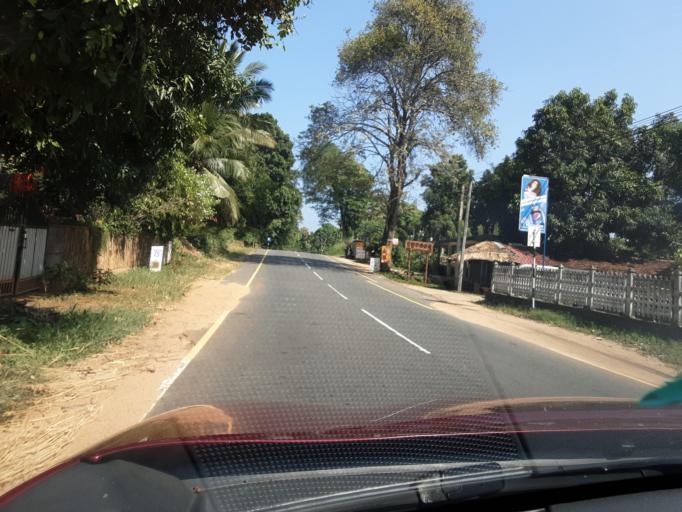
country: LK
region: Uva
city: Badulla
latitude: 7.1786
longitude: 81.0482
